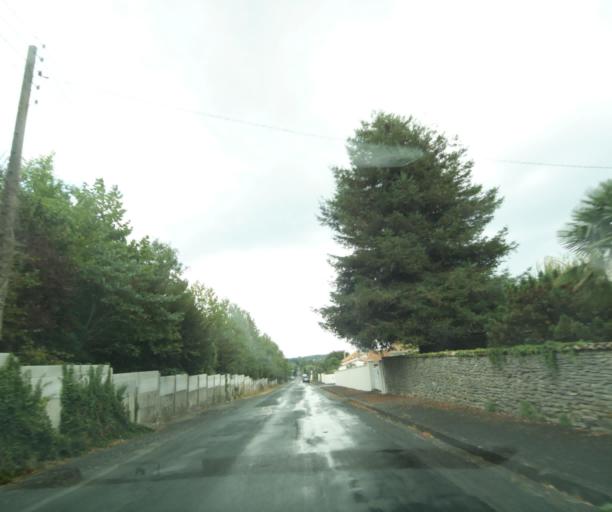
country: FR
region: Poitou-Charentes
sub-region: Departement de la Charente-Maritime
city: Tonnay-Charente
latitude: 45.9437
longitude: -0.8822
